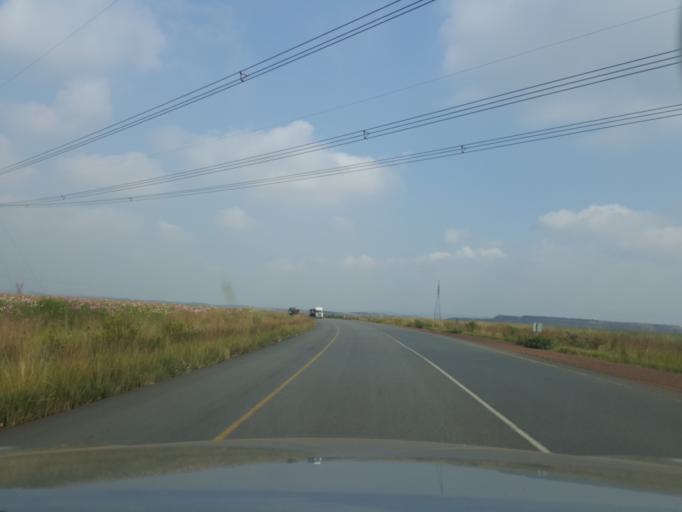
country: ZA
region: Mpumalanga
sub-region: Nkangala District Municipality
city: Witbank
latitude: -26.0158
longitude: 29.4200
